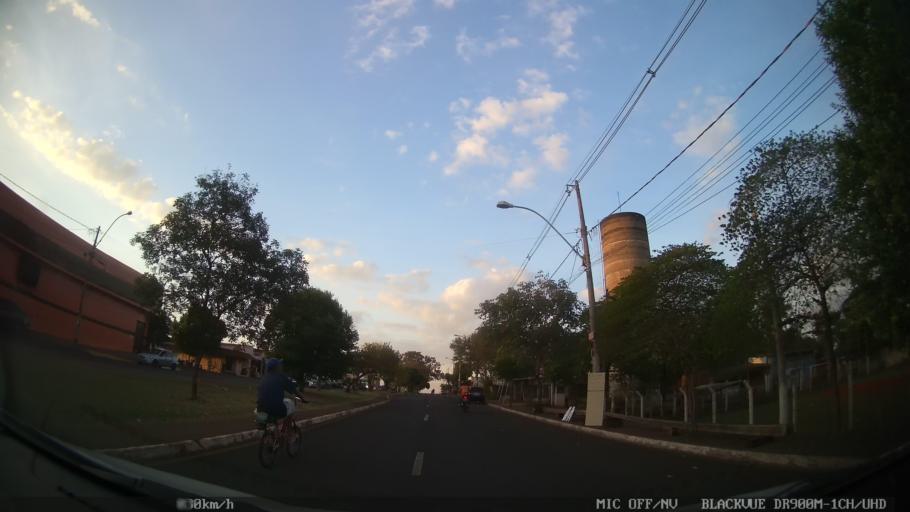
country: BR
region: Sao Paulo
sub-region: Ribeirao Preto
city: Ribeirao Preto
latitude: -21.1243
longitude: -47.8251
